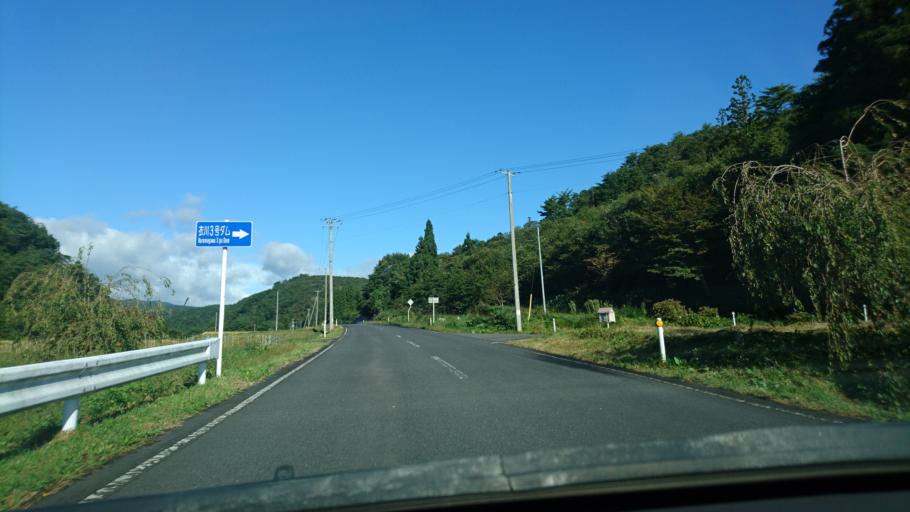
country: JP
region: Iwate
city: Ichinoseki
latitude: 39.0205
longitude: 141.0222
